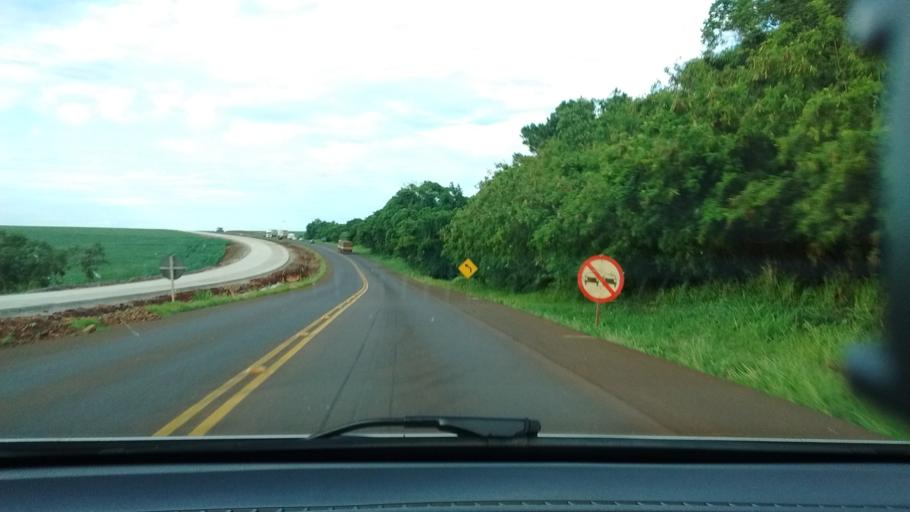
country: BR
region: Parana
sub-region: Cascavel
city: Cascavel
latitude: -25.0639
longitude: -53.5665
